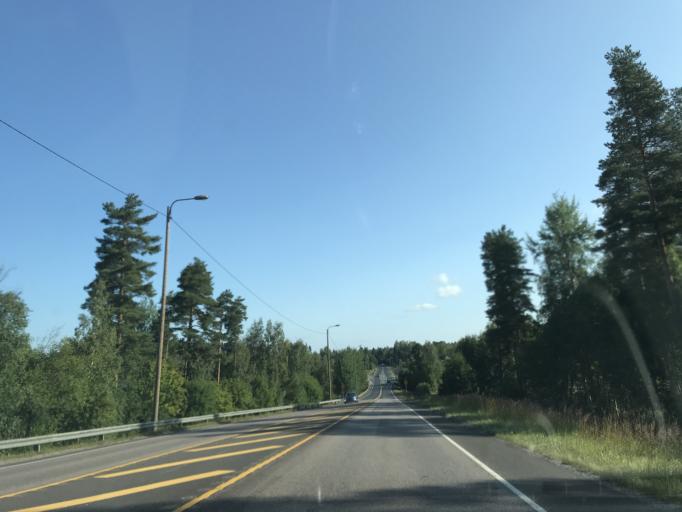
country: FI
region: Paijanne Tavastia
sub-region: Lahti
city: Lahti
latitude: 61.0477
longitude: 25.6654
